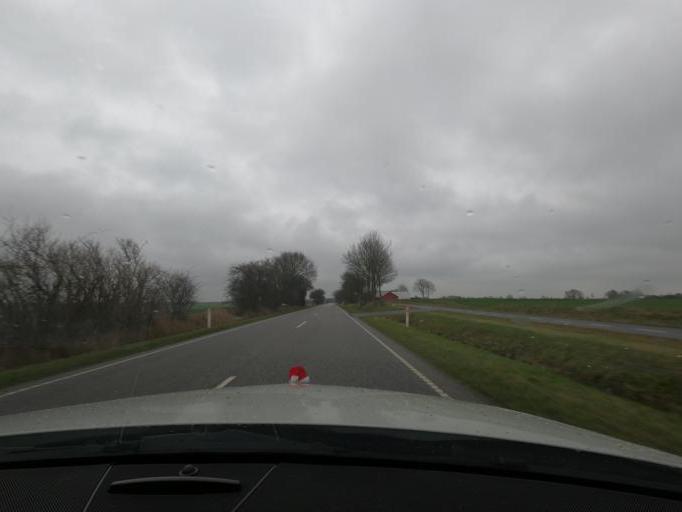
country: DK
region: South Denmark
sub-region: Haderslev Kommune
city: Starup
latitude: 55.2549
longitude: 9.6153
